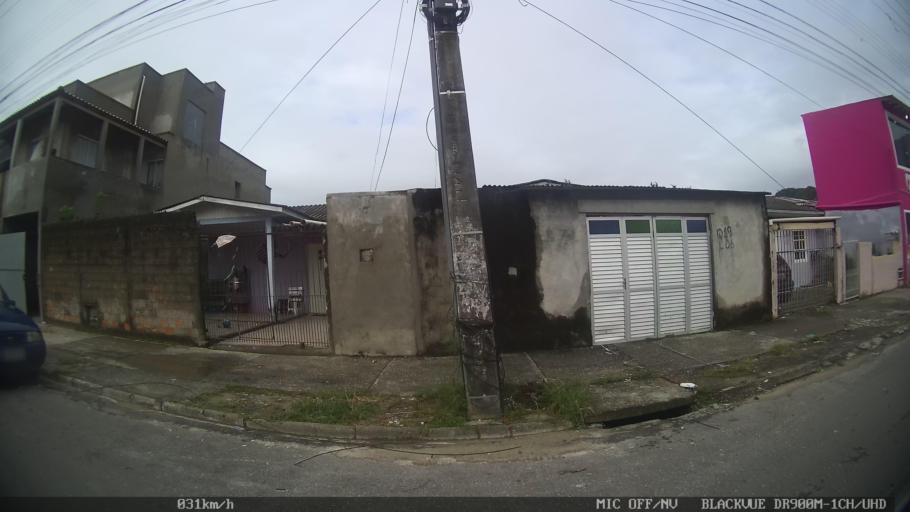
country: BR
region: Santa Catarina
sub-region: Biguacu
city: Biguacu
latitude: -27.5421
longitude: -48.6449
